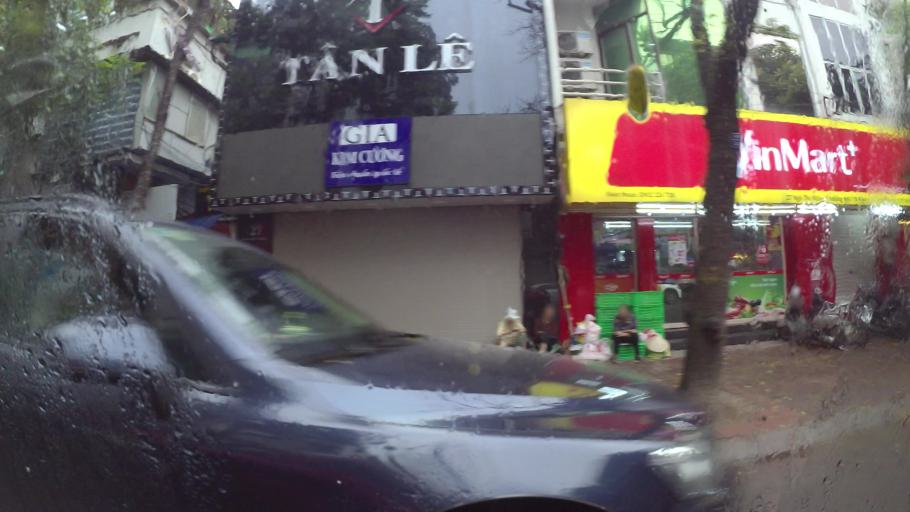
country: VN
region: Ha Noi
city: Hai BaTrung
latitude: 21.0173
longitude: 105.8529
